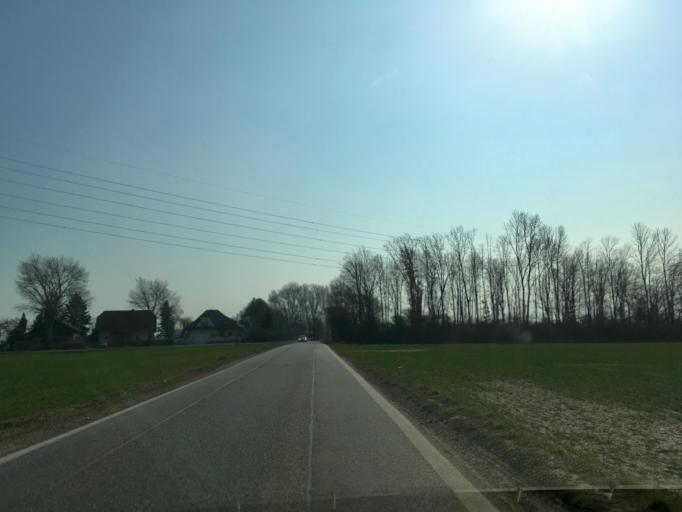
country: AT
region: Lower Austria
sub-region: Politischer Bezirk Ganserndorf
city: Gross-Enzersdorf
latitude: 48.2037
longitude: 16.4942
